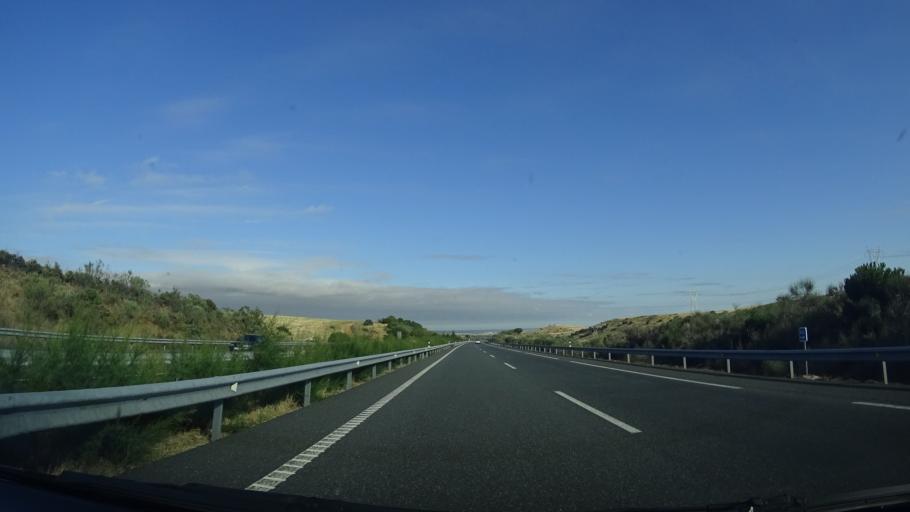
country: ES
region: Castille and Leon
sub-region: Provincia de Segovia
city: Labajos
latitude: 40.8278
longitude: -4.5200
